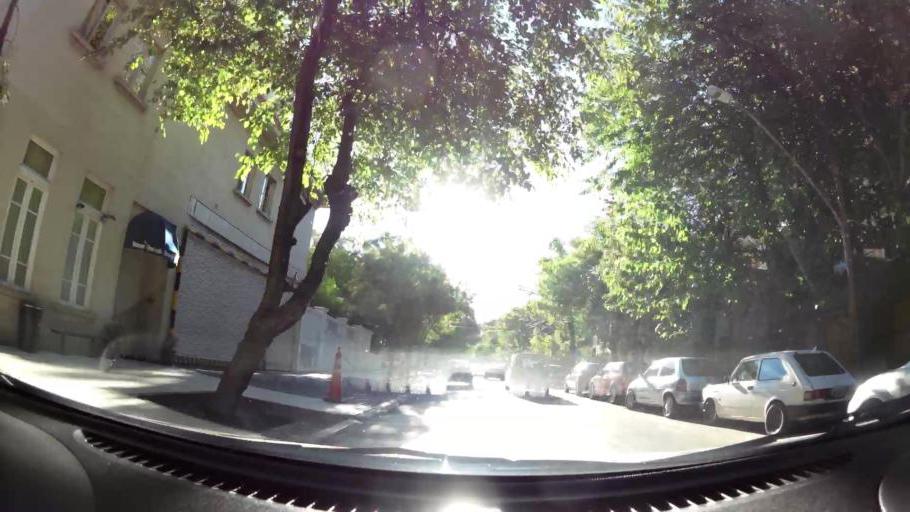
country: AR
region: Mendoza
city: Mendoza
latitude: -32.8882
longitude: -68.8463
